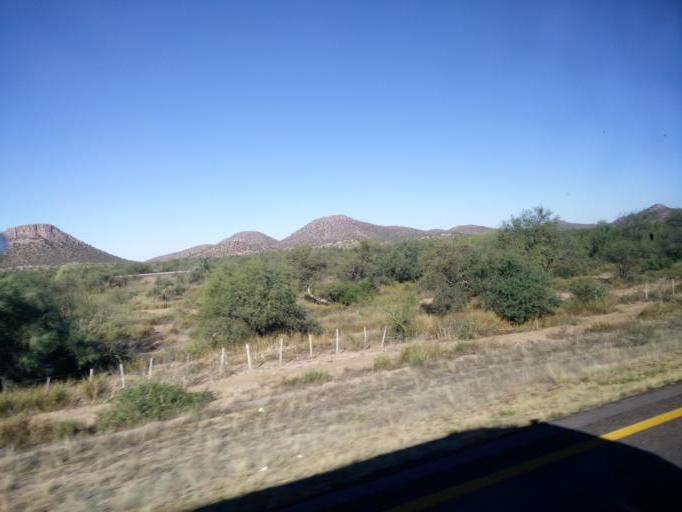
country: MX
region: Sonora
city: Hermosillo
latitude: 28.8702
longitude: -110.9585
